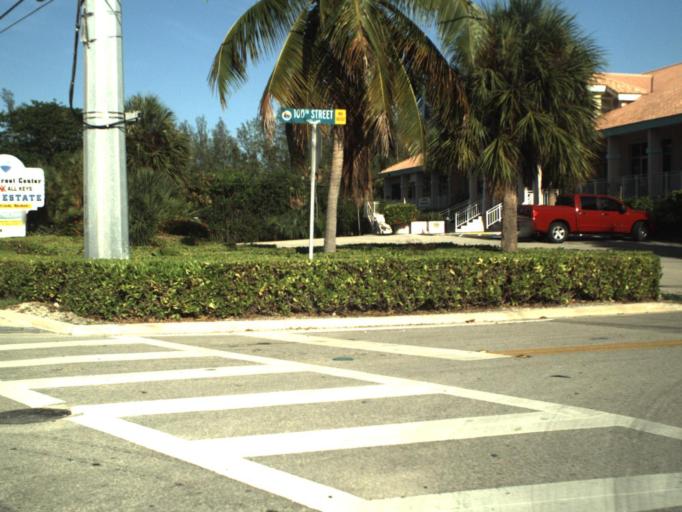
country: US
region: Florida
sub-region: Monroe County
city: Marathon
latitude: 24.7273
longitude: -81.0433
